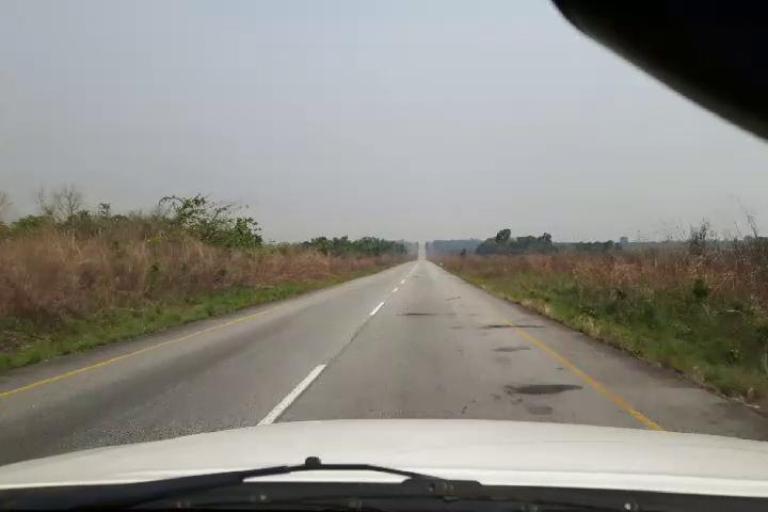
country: SL
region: Southern Province
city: Largo
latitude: 8.2386
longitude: -12.0840
